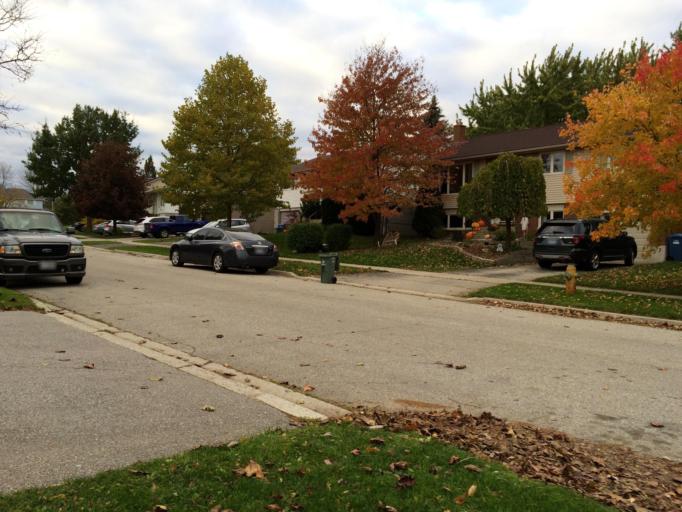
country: CA
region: Ontario
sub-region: Wellington County
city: Guelph
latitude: 43.5320
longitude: -80.2996
